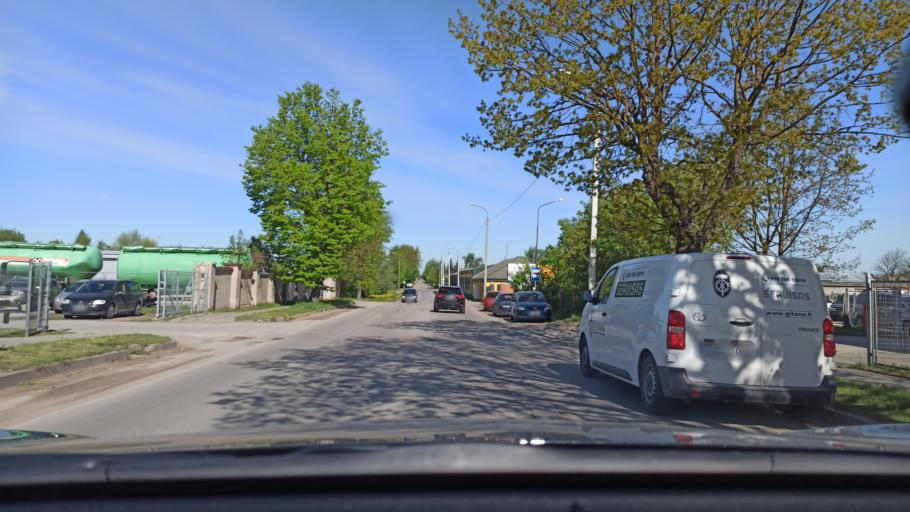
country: LT
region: Siauliu apskritis
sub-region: Siauliai
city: Siauliai
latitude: 55.9510
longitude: 23.3044
